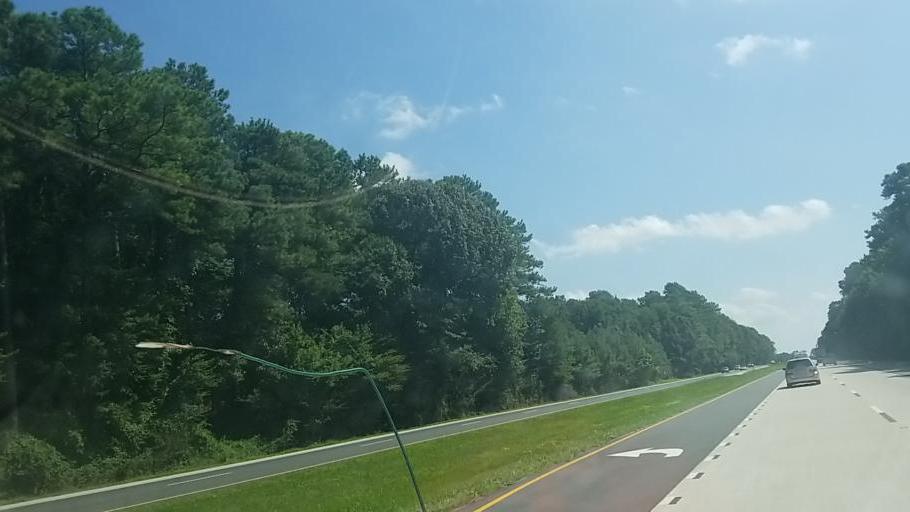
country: US
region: Delaware
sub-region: Sussex County
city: Milford
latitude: 38.8665
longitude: -75.4395
